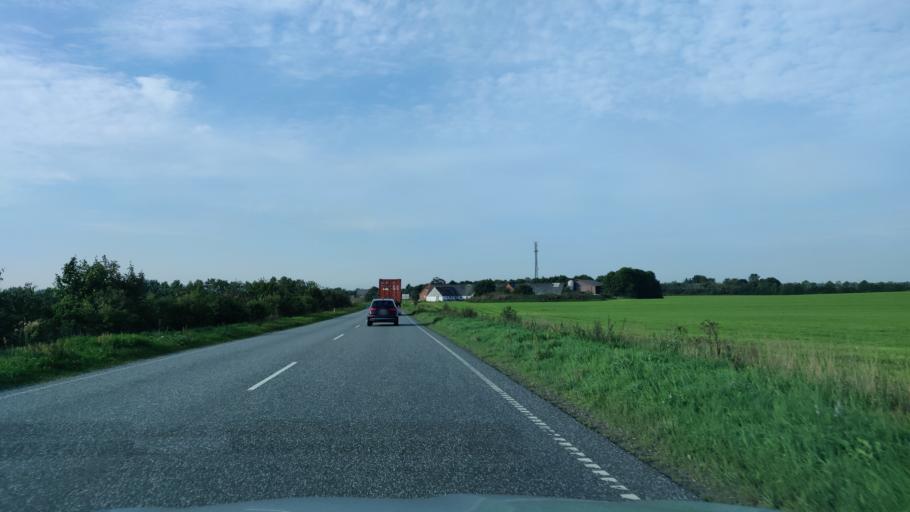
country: DK
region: North Denmark
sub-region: Vesthimmerland Kommune
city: Aars
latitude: 56.7766
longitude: 9.5769
